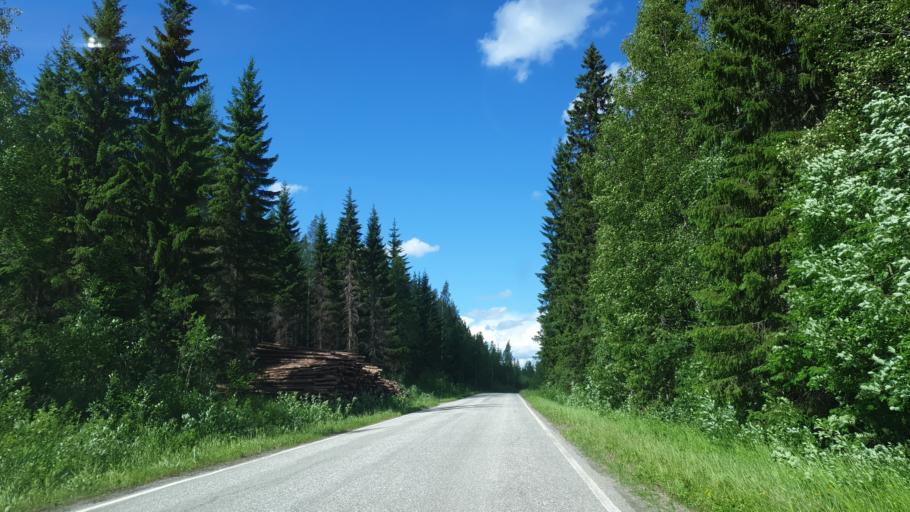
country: FI
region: Northern Savo
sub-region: Koillis-Savo
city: Kaavi
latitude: 63.0291
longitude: 28.6115
